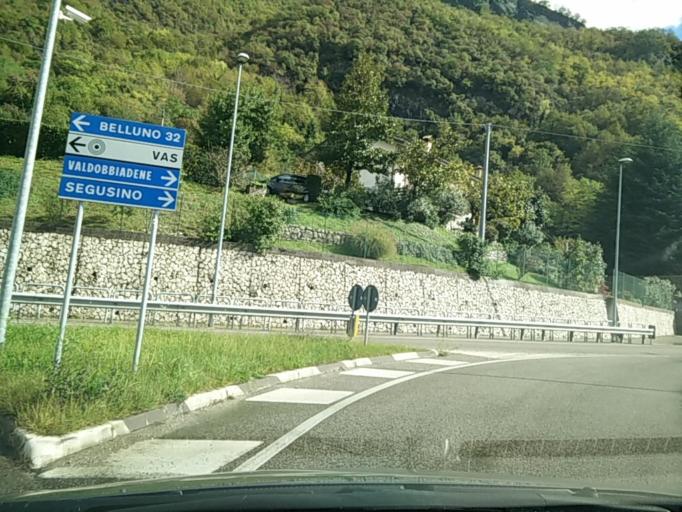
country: IT
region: Veneto
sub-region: Provincia di Belluno
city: Vas
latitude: 45.9331
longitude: 11.9396
